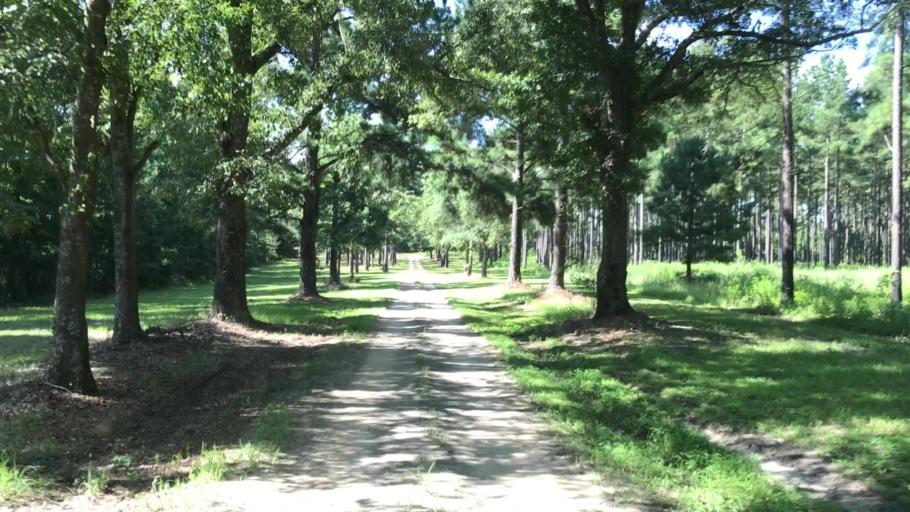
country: US
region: Georgia
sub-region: Jefferson County
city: Wadley
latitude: 32.8120
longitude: -82.3342
